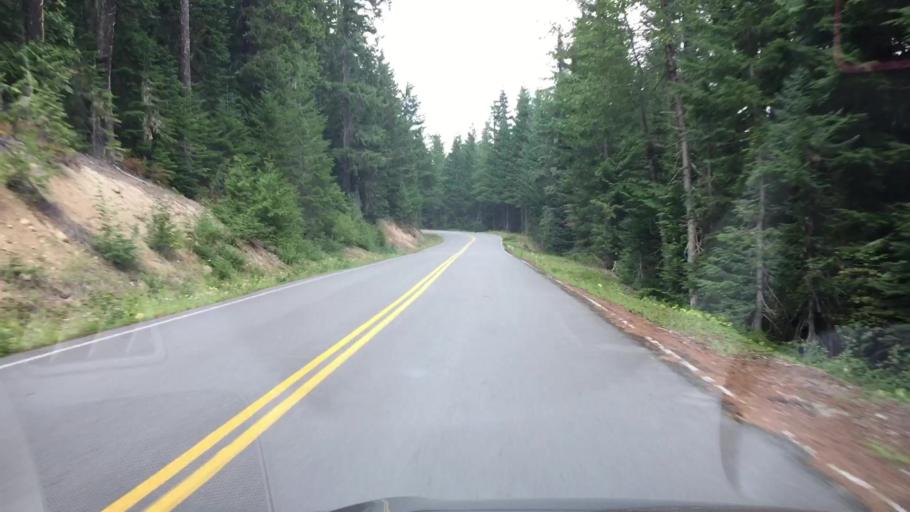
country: US
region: Washington
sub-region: Klickitat County
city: White Salmon
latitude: 46.1472
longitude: -121.6268
